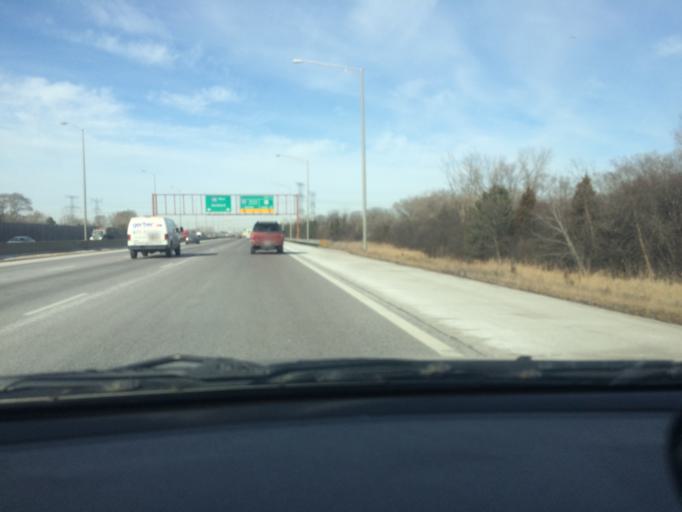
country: US
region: Illinois
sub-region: DuPage County
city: Itasca
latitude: 41.9525
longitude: -88.0111
